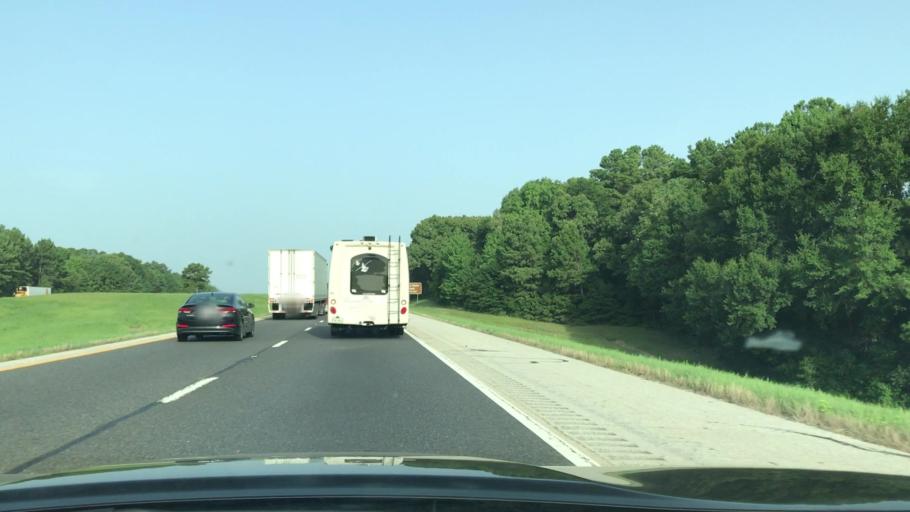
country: US
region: Texas
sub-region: Smith County
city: Tyler
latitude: 32.4528
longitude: -95.2568
